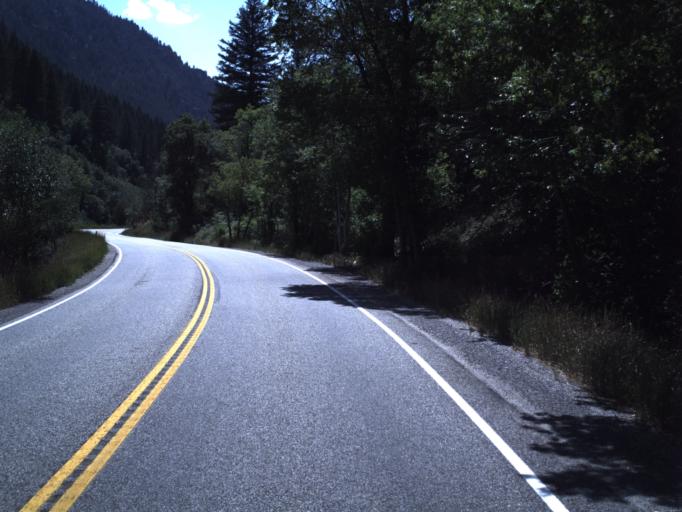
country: US
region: Utah
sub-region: Cache County
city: North Logan
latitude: 41.8105
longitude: -111.6260
